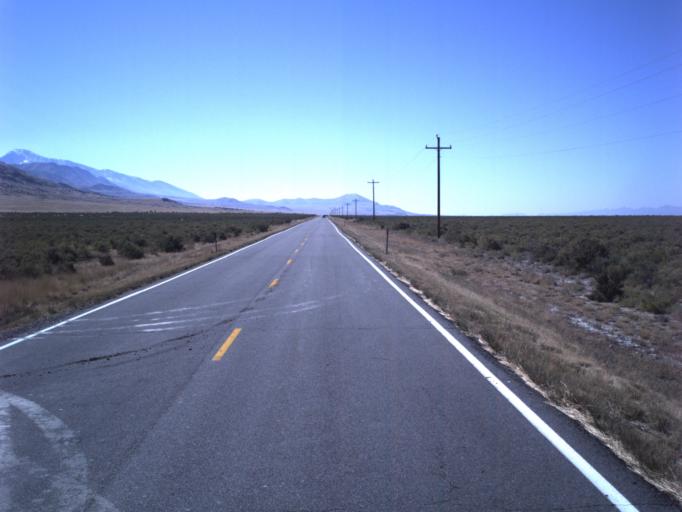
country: US
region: Utah
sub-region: Tooele County
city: Grantsville
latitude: 40.7122
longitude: -112.6625
